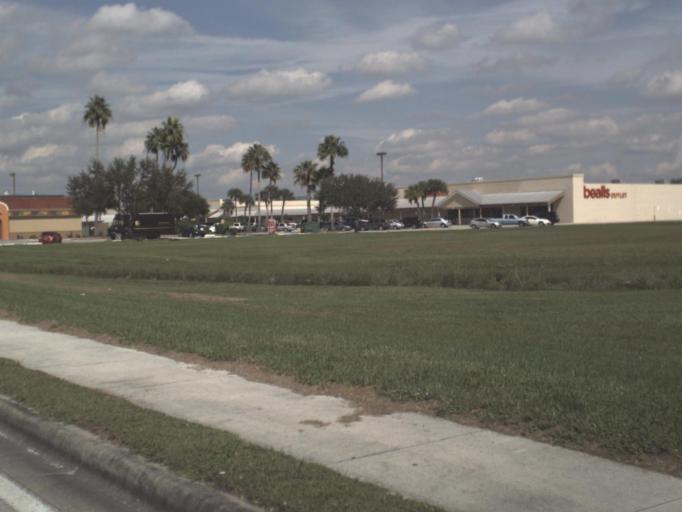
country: US
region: Florida
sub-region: Okeechobee County
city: Okeechobee
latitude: 27.2112
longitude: -80.8298
